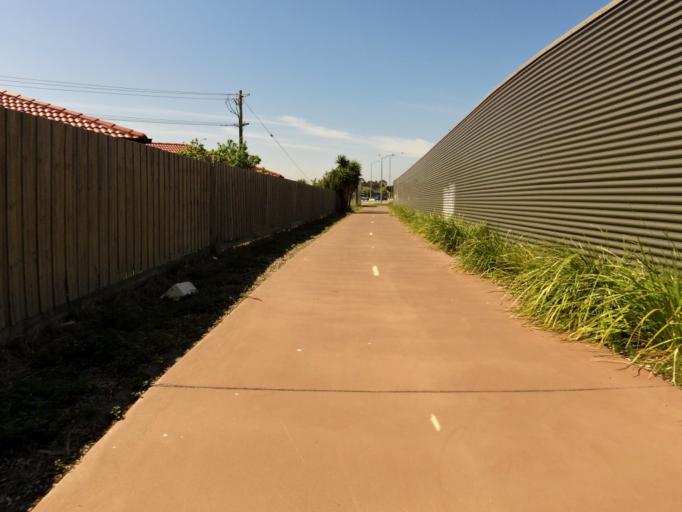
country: AU
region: Victoria
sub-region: Monash
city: Oakleigh South
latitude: -37.9431
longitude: 145.0962
